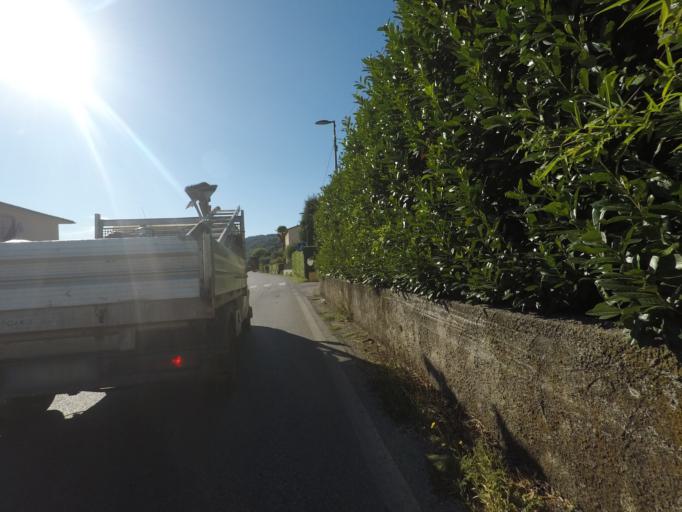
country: IT
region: Tuscany
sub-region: Provincia di Lucca
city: San Martino in Freddana-Monsagrati
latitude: 43.9095
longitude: 10.4375
